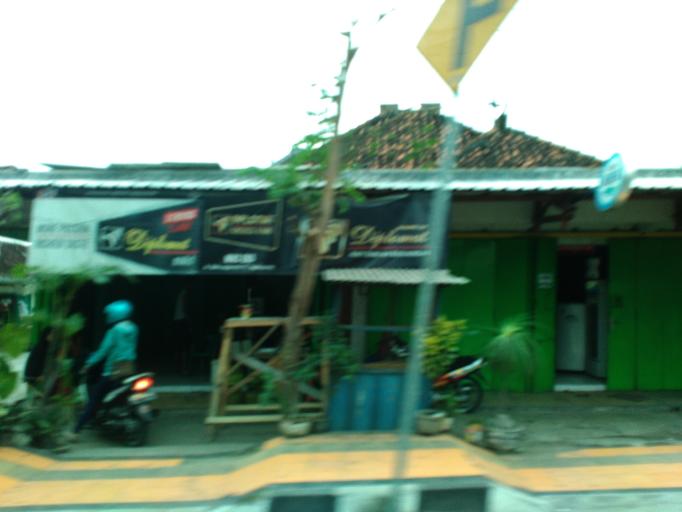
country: ID
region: Central Java
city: Gatak
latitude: -7.5961
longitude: 110.7032
